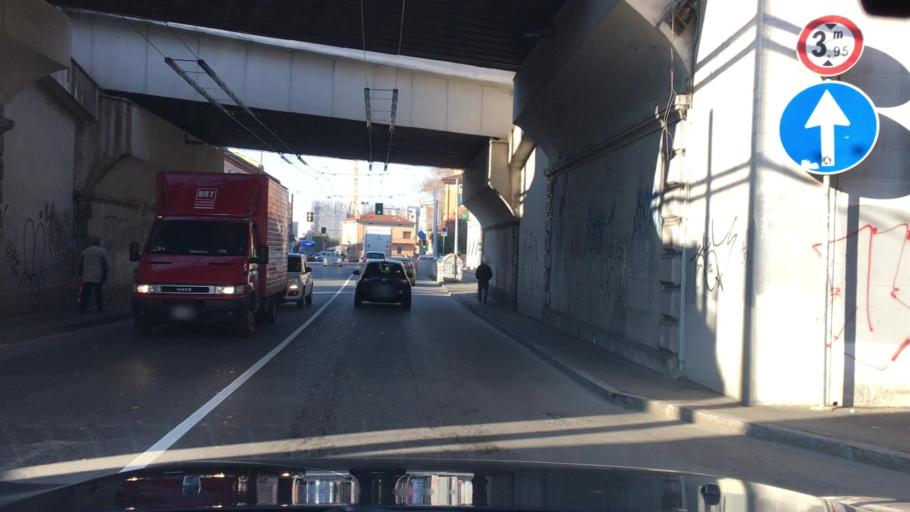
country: IT
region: Emilia-Romagna
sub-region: Provincia di Bologna
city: Bologna
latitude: 44.4933
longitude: 11.3755
